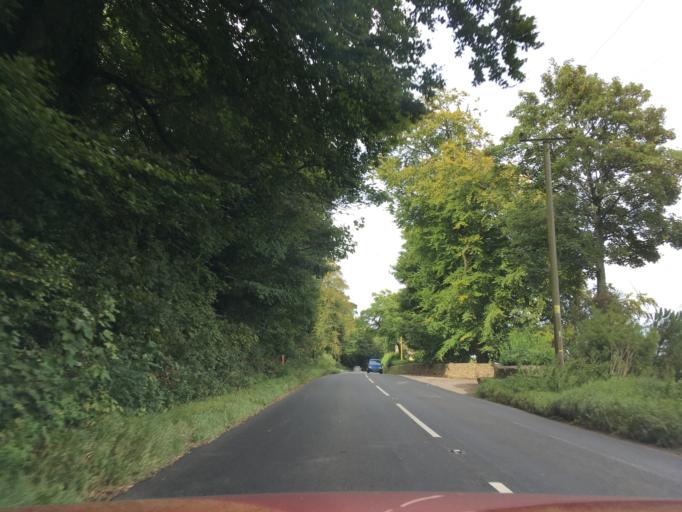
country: GB
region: England
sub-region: Gloucestershire
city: Nailsworth
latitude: 51.6803
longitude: -2.2761
